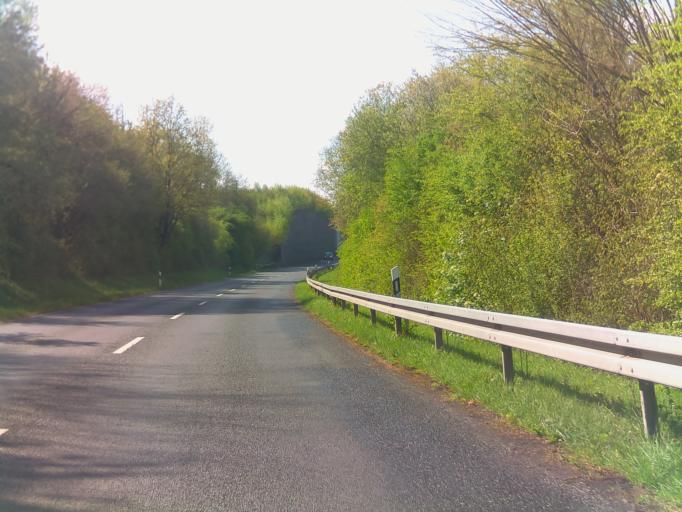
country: DE
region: Hesse
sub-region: Regierungsbezirk Giessen
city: Wetzlar
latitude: 50.5714
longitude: 8.5517
